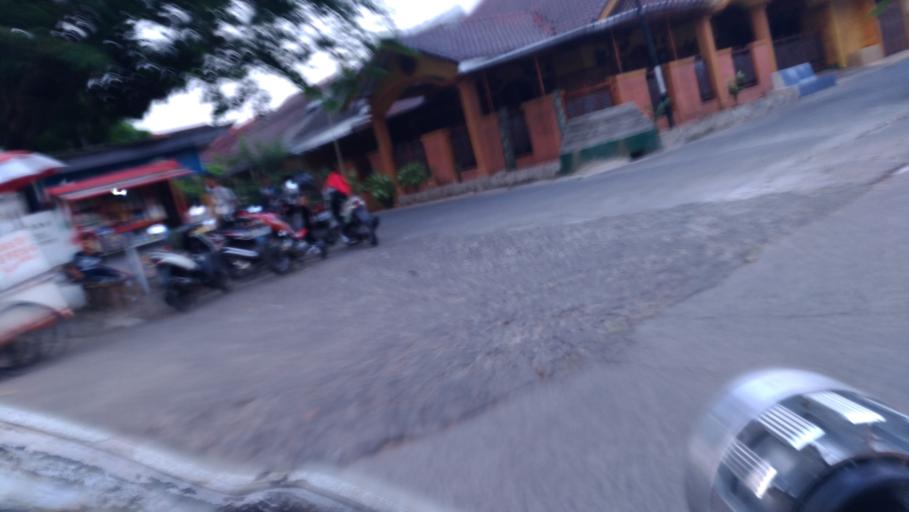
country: ID
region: West Java
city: Depok
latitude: -6.3610
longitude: 106.8648
